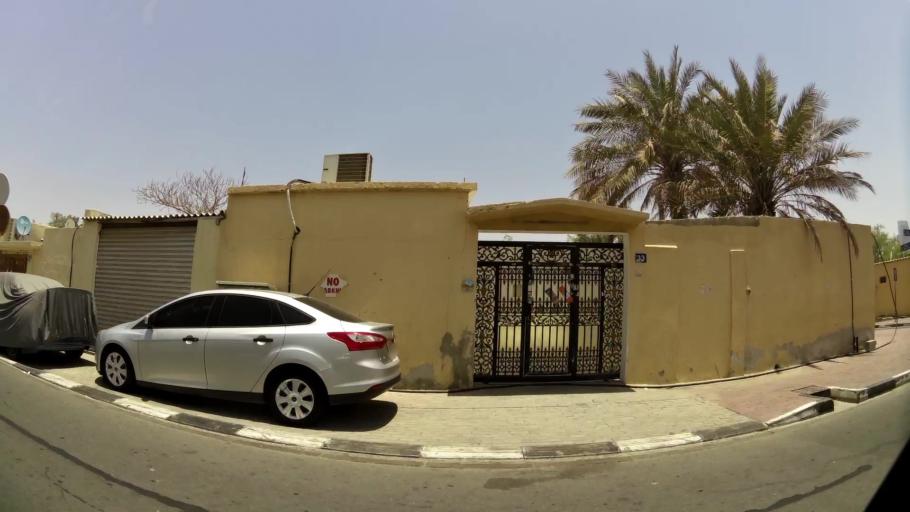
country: AE
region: Ash Shariqah
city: Sharjah
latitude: 25.2410
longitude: 55.2830
